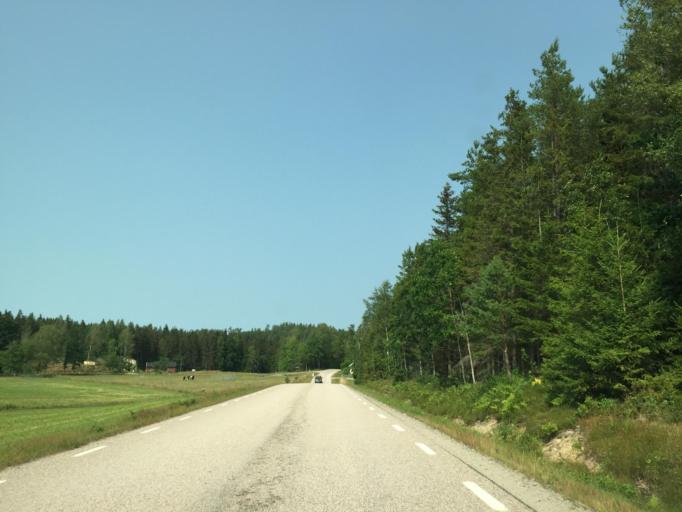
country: SE
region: Vaestra Goetaland
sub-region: Lilla Edets Kommun
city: Lilla Edet
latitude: 58.1628
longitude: 12.0714
